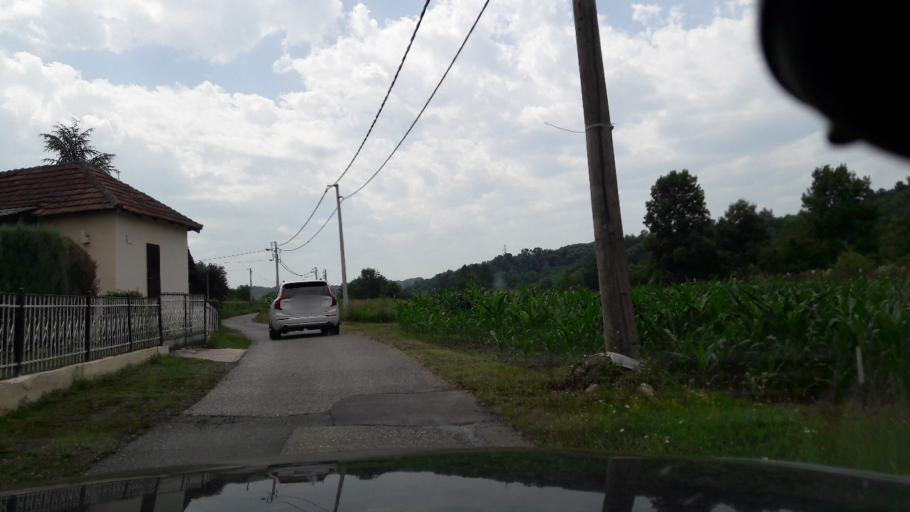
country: RS
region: Central Serbia
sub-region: Belgrade
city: Sopot
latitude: 44.6337
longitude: 20.5924
